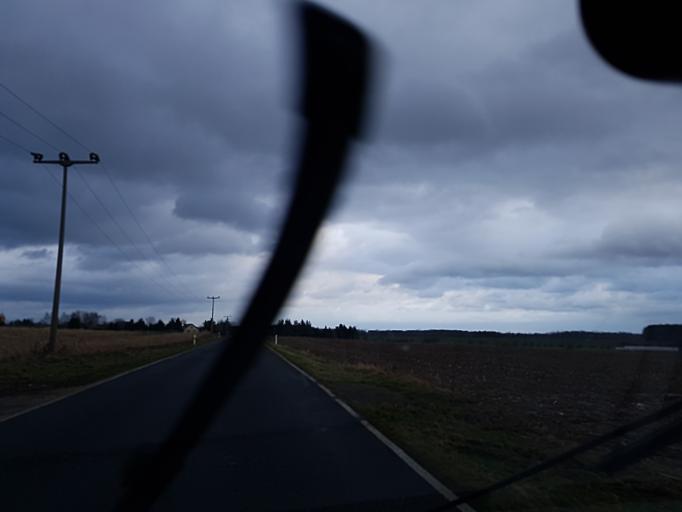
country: DE
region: Brandenburg
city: Hohenleipisch
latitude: 51.4864
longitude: 13.5295
